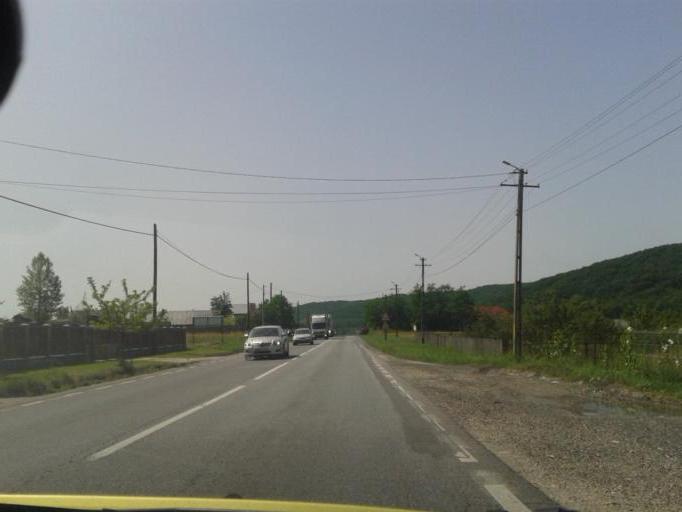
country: RO
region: Arges
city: Draganu-Olteni
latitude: 44.9181
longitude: 24.7210
